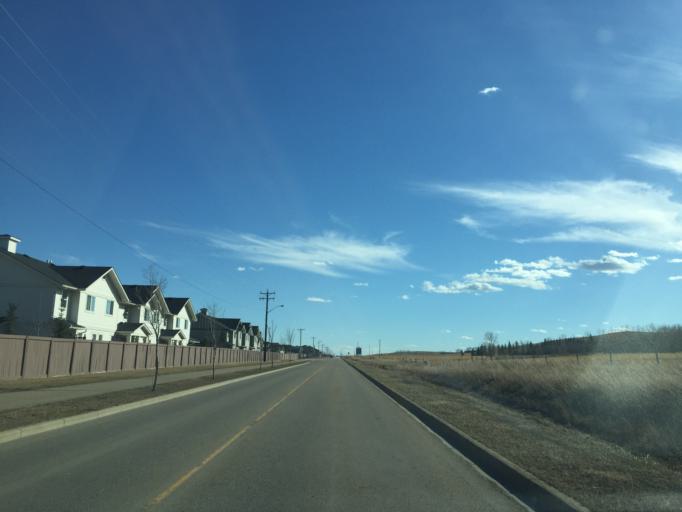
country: CA
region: Alberta
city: Airdrie
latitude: 51.2924
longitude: -114.0486
